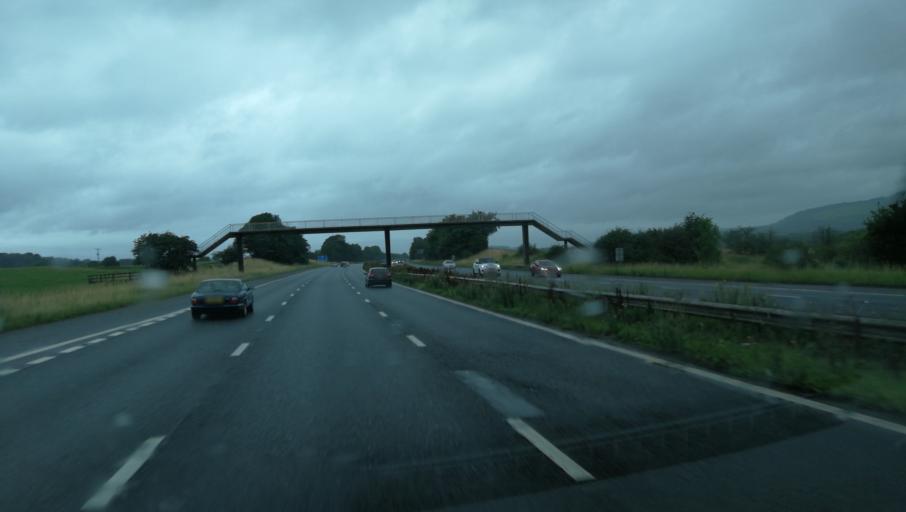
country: GB
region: England
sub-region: Borough of Bolton
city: Horwich
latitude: 53.5790
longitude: -2.5520
